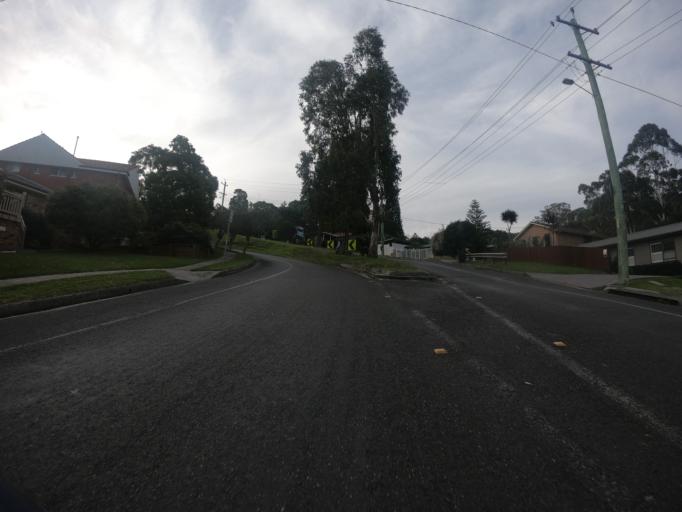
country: AU
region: New South Wales
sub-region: Wollongong
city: West Wollongong
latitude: -34.4358
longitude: 150.8543
